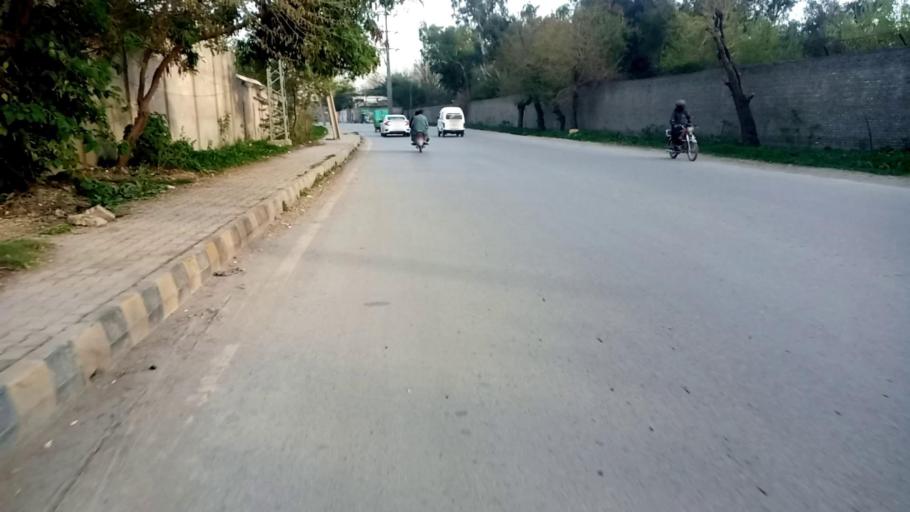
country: PK
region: Khyber Pakhtunkhwa
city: Peshawar
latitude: 34.0205
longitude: 71.5652
